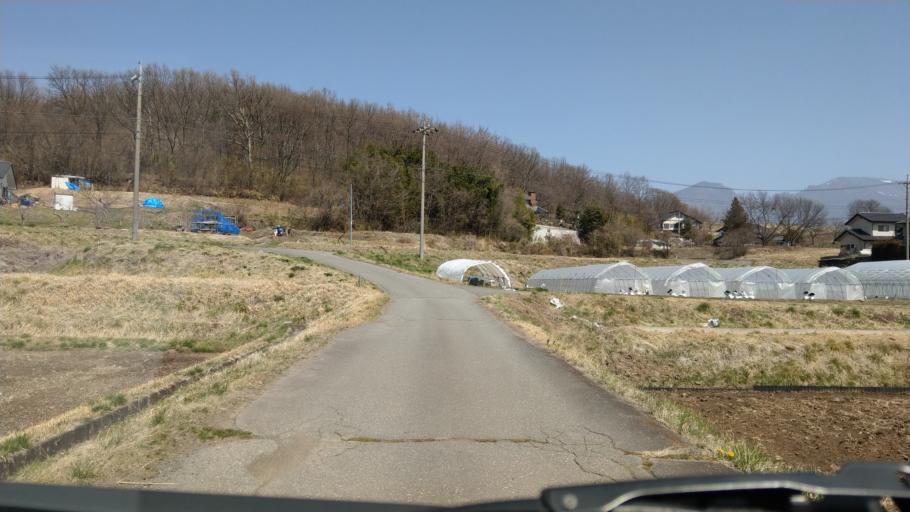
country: JP
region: Nagano
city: Komoro
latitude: 36.3047
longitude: 138.4356
